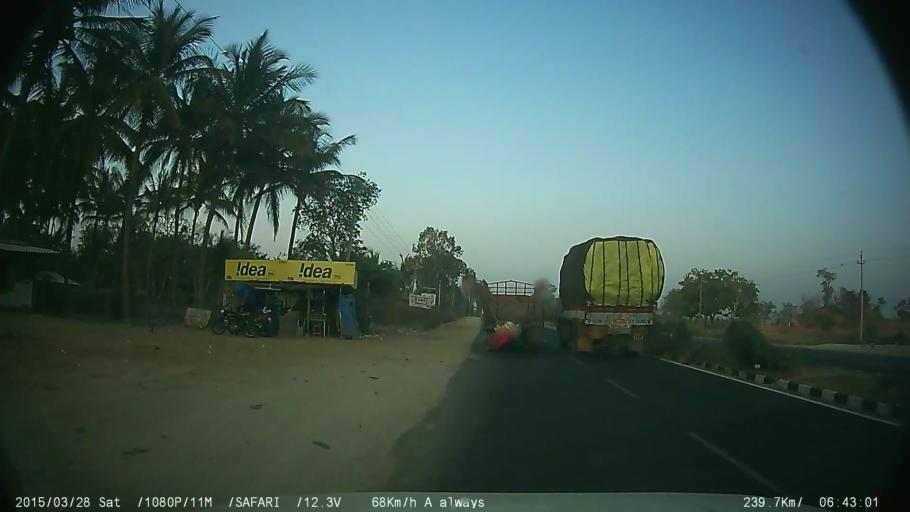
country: IN
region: Karnataka
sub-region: Ramanagara
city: Channapatna
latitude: 12.6351
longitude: 77.1228
